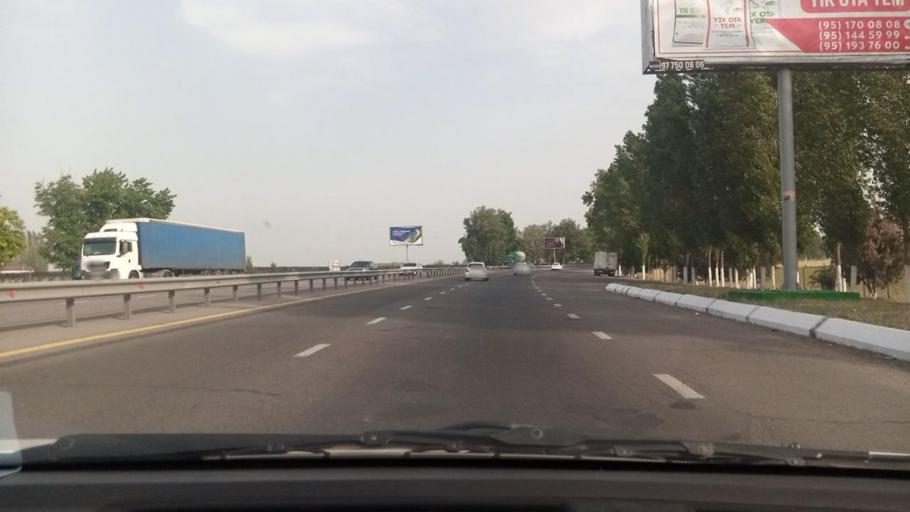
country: UZ
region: Toshkent Shahri
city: Bektemir
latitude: 41.2407
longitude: 69.4007
